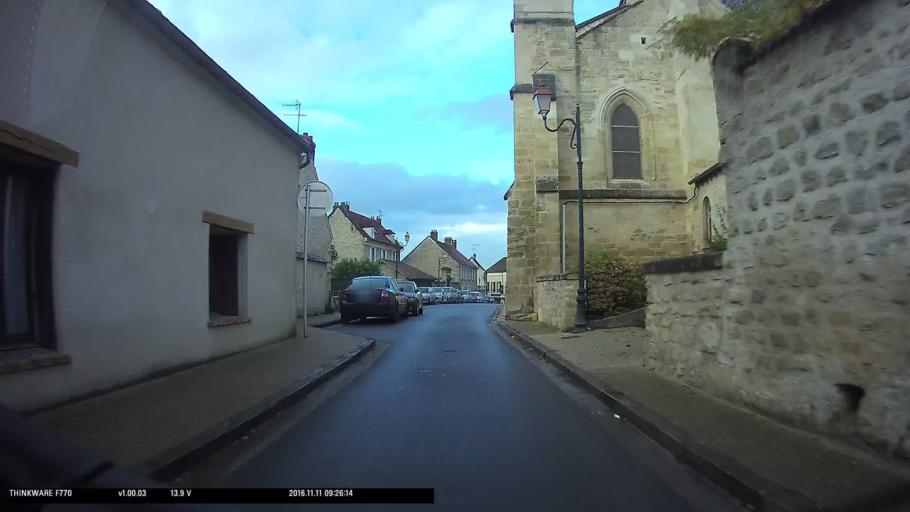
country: FR
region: Ile-de-France
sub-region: Departement du Val-d'Oise
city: Osny
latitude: 49.0774
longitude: 2.0318
